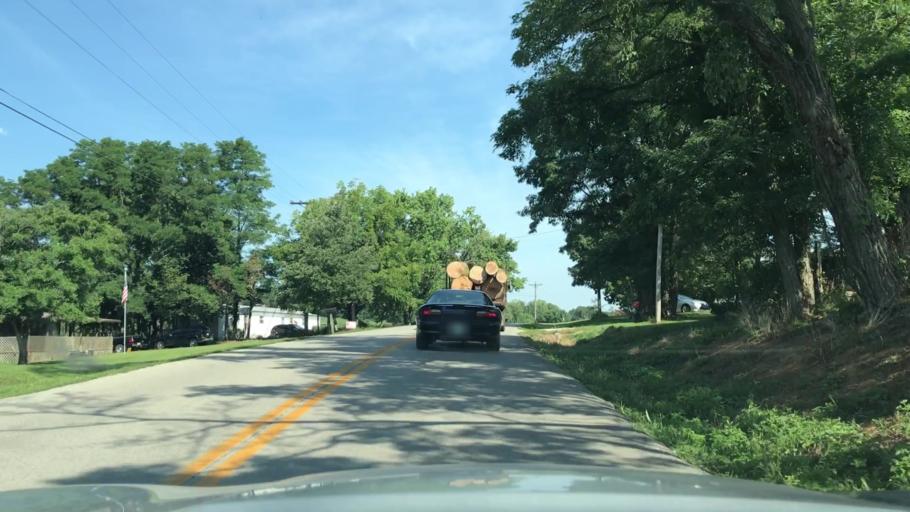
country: US
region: Kentucky
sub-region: Clinton County
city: Albany
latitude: 36.7533
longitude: -84.9953
